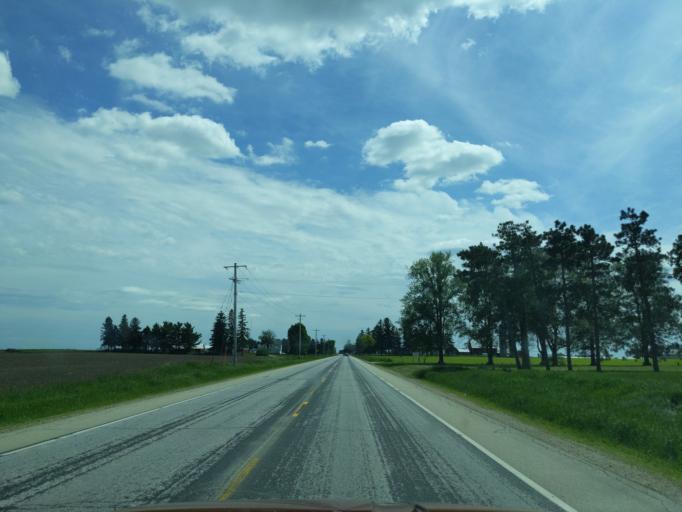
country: US
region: Wisconsin
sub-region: Dane County
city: De Forest
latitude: 43.3173
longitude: -89.3254
